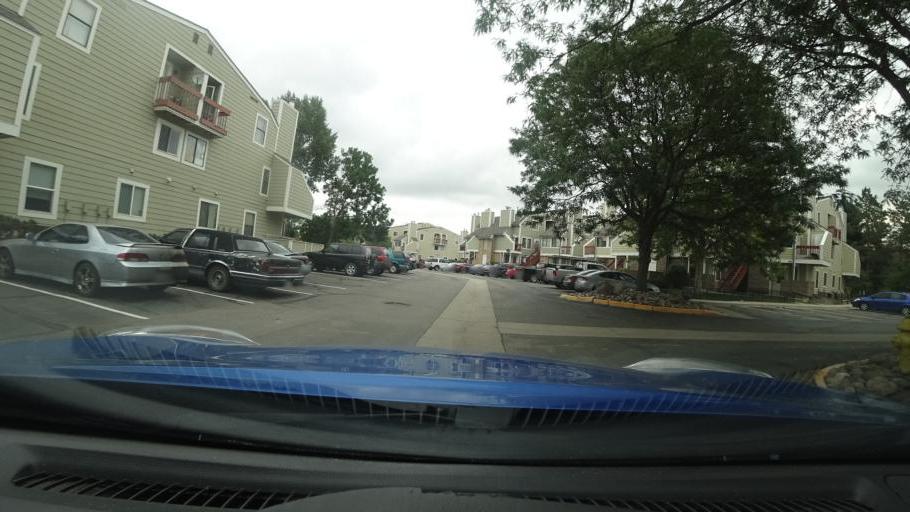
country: US
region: Colorado
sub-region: Adams County
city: Aurora
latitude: 39.6991
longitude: -104.8178
